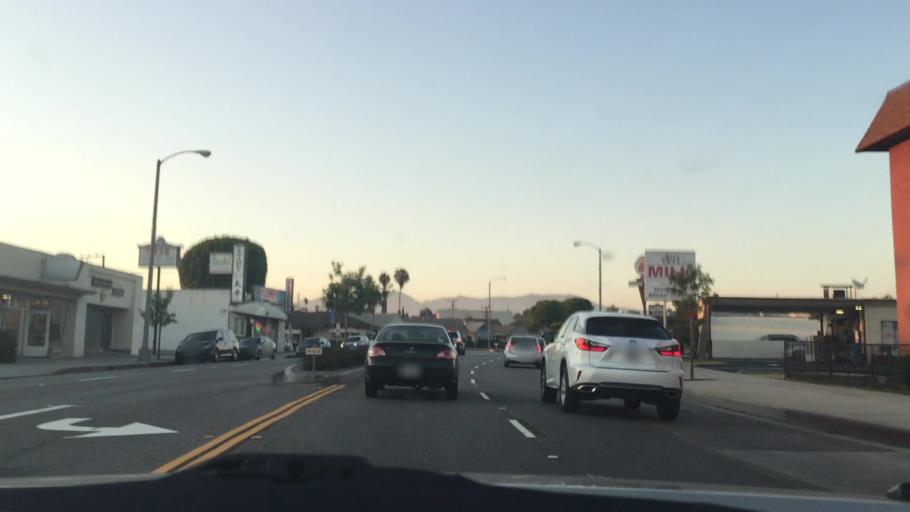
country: US
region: California
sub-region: Los Angeles County
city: Monterey Park
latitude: 34.0371
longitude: -118.1304
